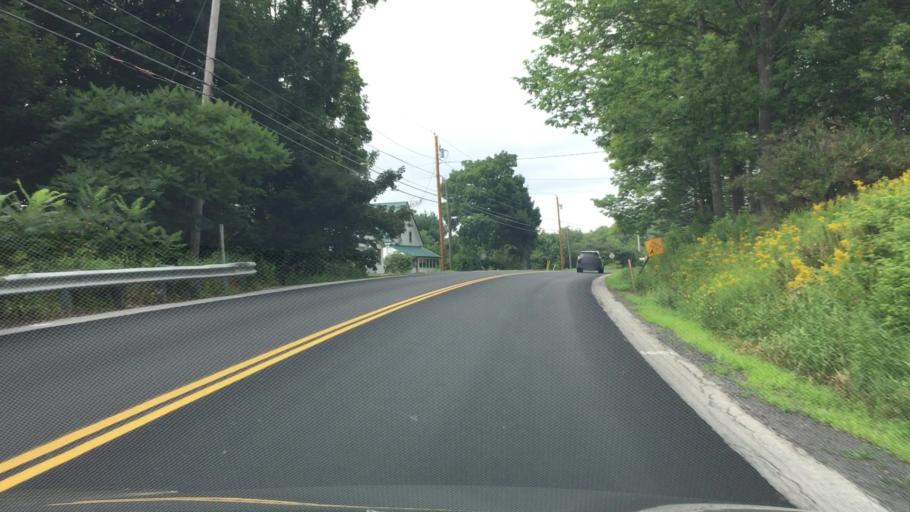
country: US
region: Maine
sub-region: Waldo County
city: Winterport
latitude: 44.6201
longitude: -68.8310
